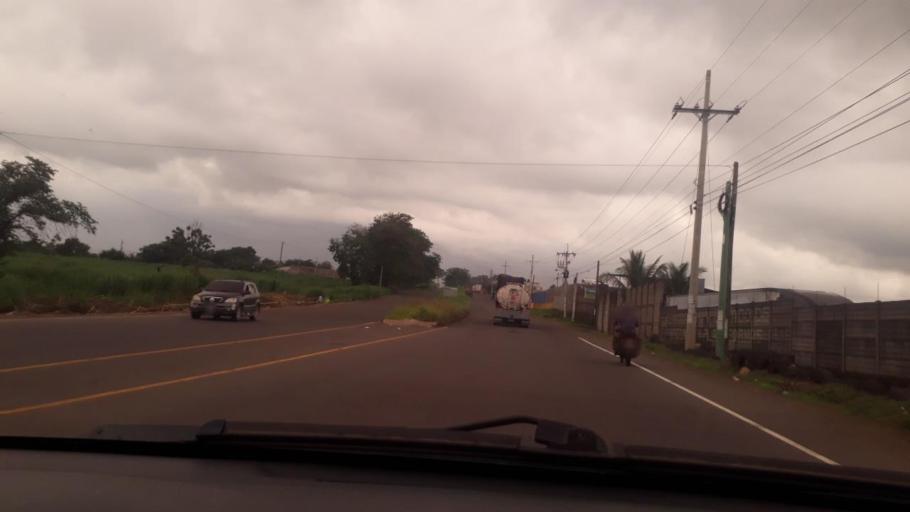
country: GT
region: Escuintla
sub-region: Municipio de Escuintla
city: Escuintla
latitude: 14.2760
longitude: -90.7606
